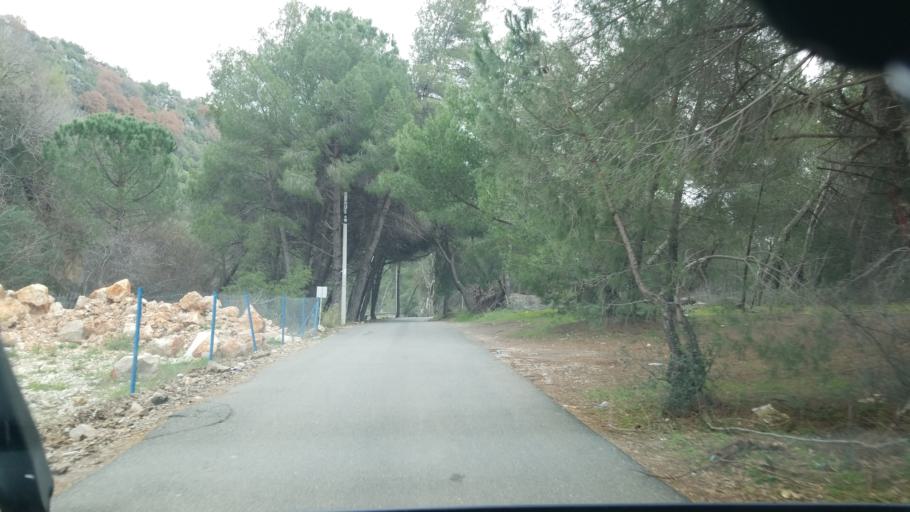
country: AL
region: Lezhe
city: Shengjin
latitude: 41.8244
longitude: 19.5593
